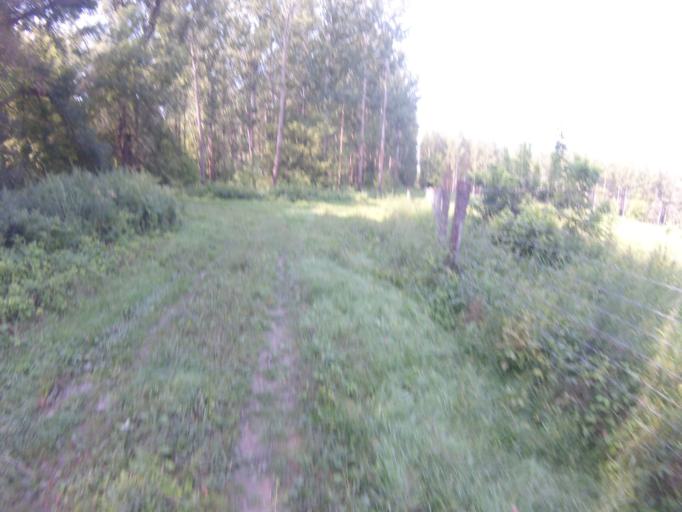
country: HU
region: Bacs-Kiskun
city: Baja
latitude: 46.2024
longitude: 18.8951
